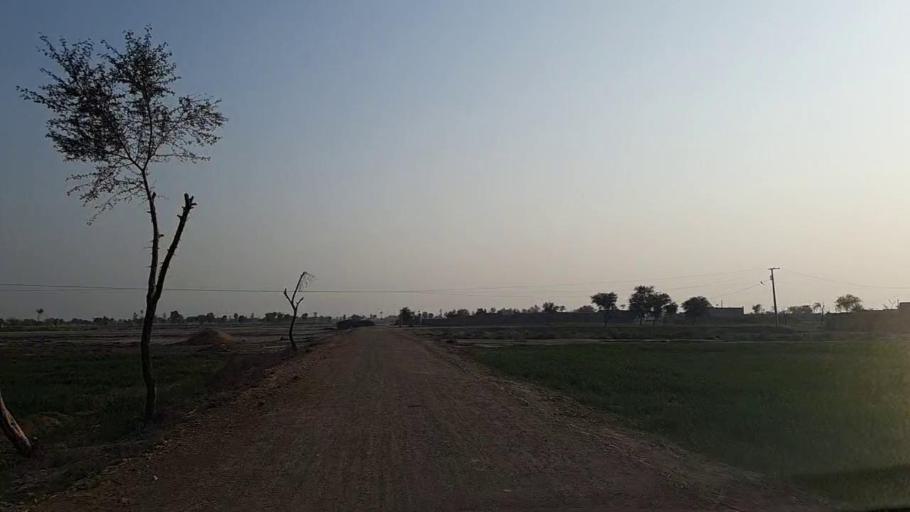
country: PK
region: Sindh
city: Daur
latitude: 26.3953
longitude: 68.3916
